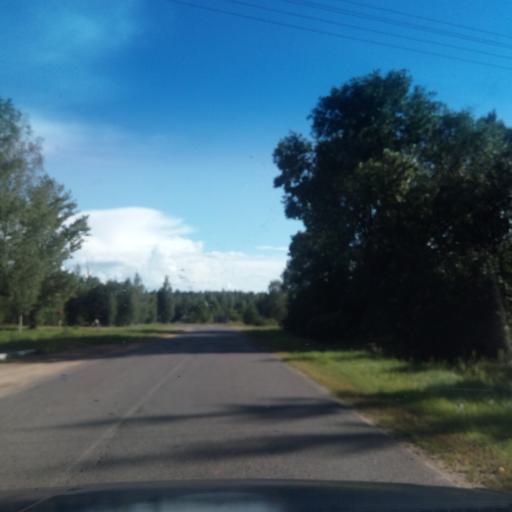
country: BY
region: Vitebsk
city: Dzisna
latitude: 55.6552
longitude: 28.3222
